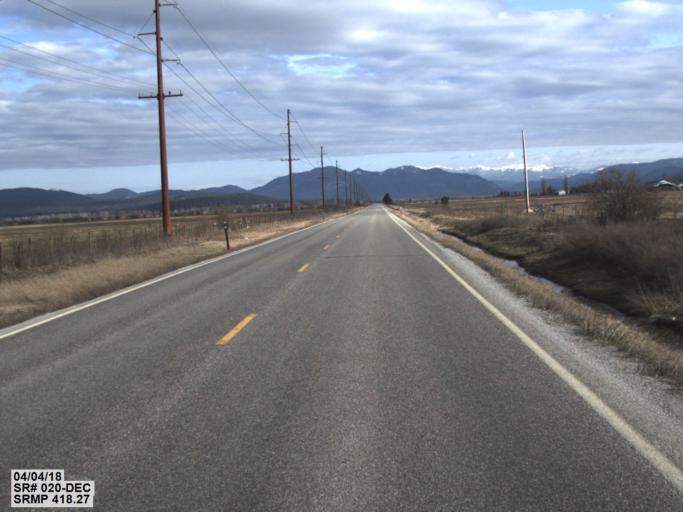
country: US
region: Washington
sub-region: Pend Oreille County
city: Newport
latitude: 48.3484
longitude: -117.3045
